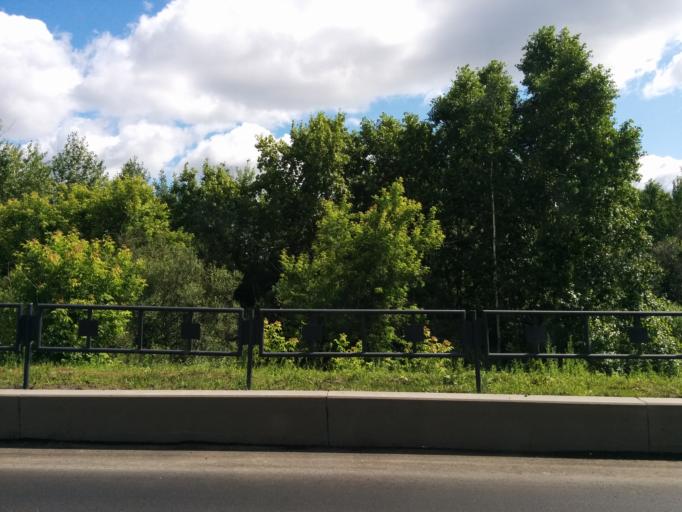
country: RU
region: Perm
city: Perm
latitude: 58.0263
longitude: 56.2185
